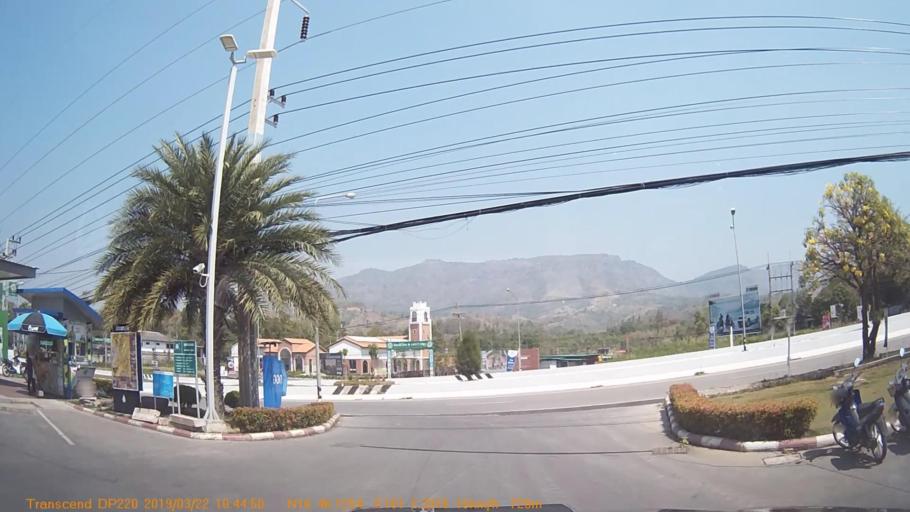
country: TH
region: Phetchabun
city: Khao Kho
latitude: 16.7688
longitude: 101.0399
